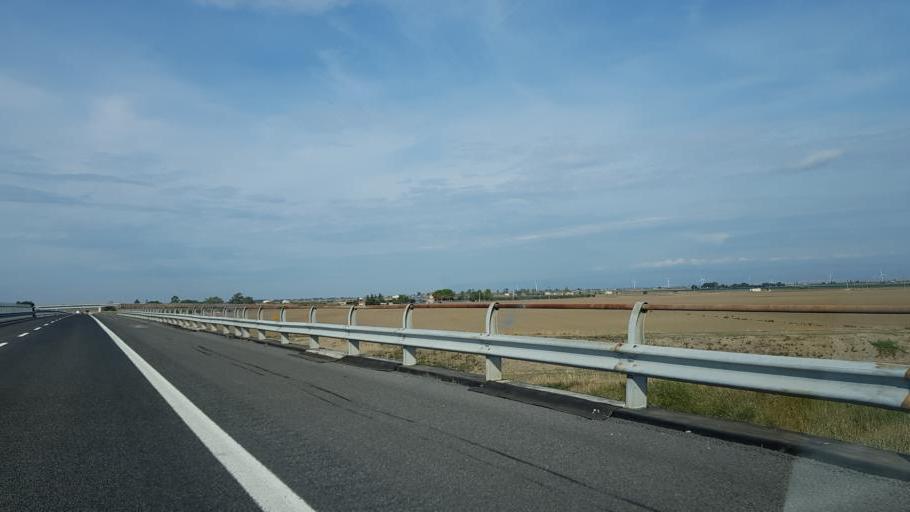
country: IT
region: Apulia
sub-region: Provincia di Foggia
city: Carapelle
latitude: 41.3798
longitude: 15.7548
